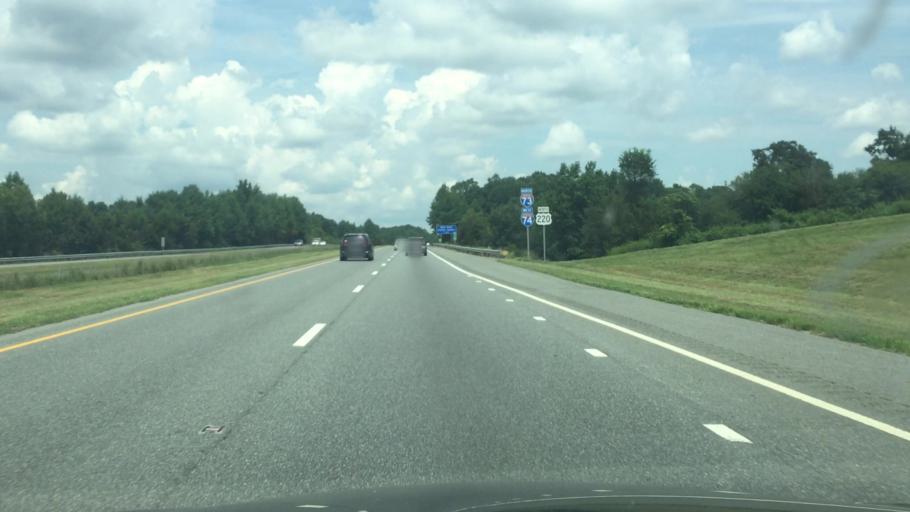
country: US
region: North Carolina
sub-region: Montgomery County
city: Biscoe
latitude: 35.4969
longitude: -79.7805
